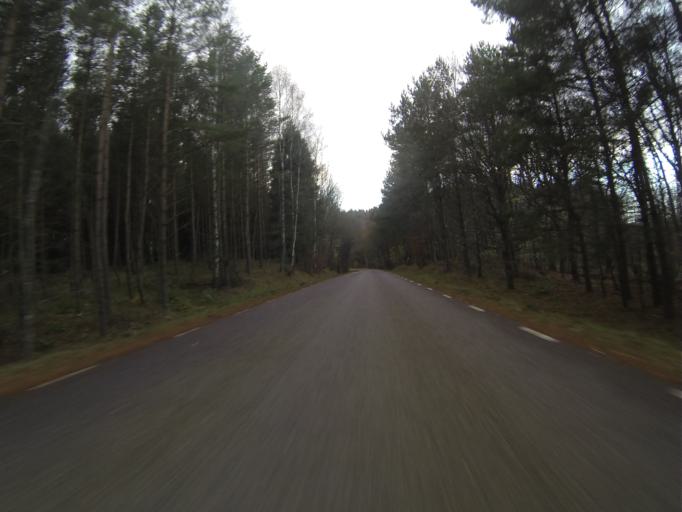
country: SE
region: Skane
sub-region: Lunds Kommun
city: Genarp
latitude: 55.5819
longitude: 13.3907
